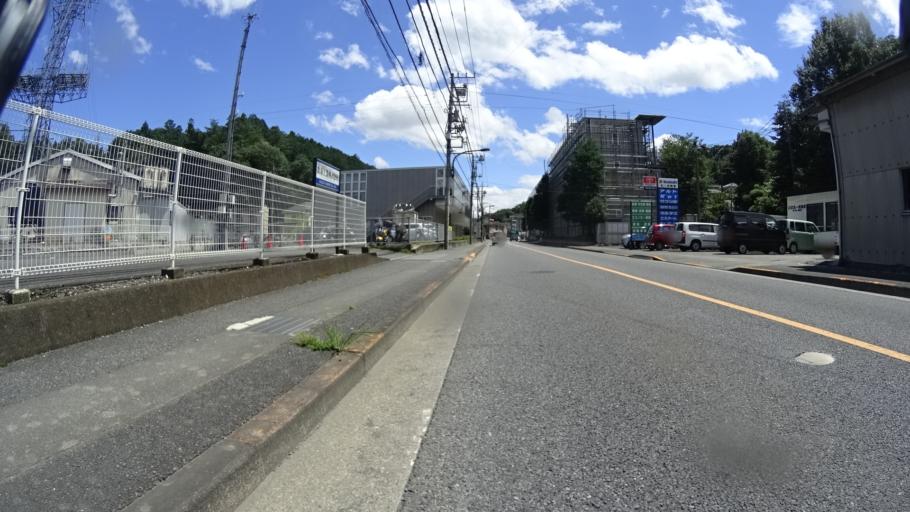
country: JP
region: Tokyo
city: Ome
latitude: 35.7965
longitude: 139.2690
